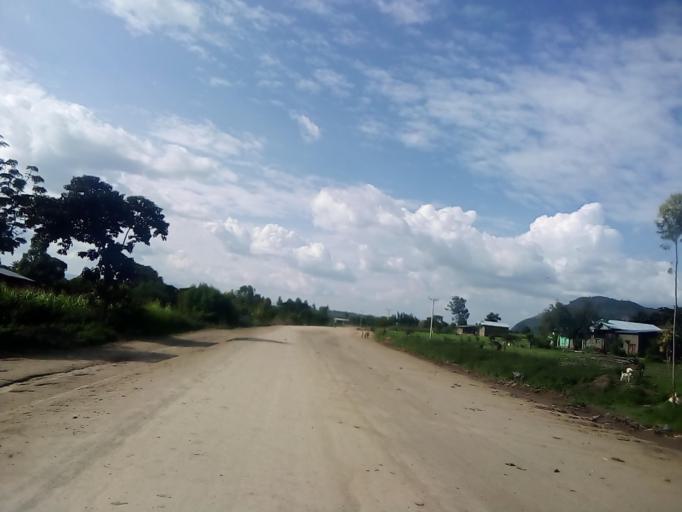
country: ET
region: Southern Nations, Nationalities, and People's Region
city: K'olito
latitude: 7.6115
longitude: 38.0654
